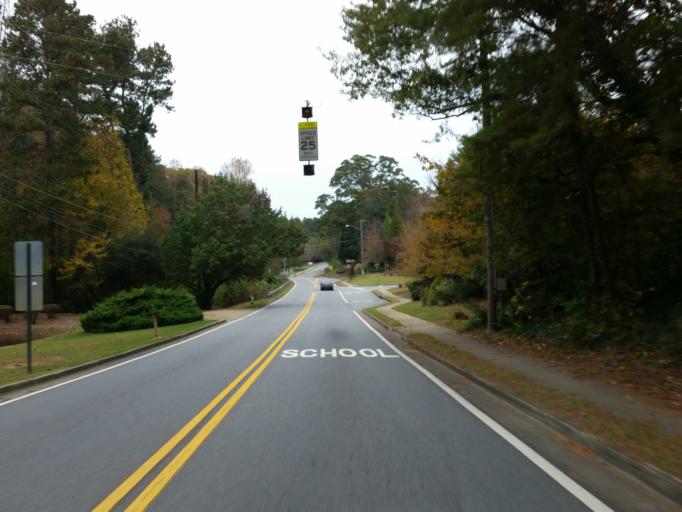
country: US
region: Georgia
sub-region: Cherokee County
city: Woodstock
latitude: 34.0302
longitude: -84.4809
